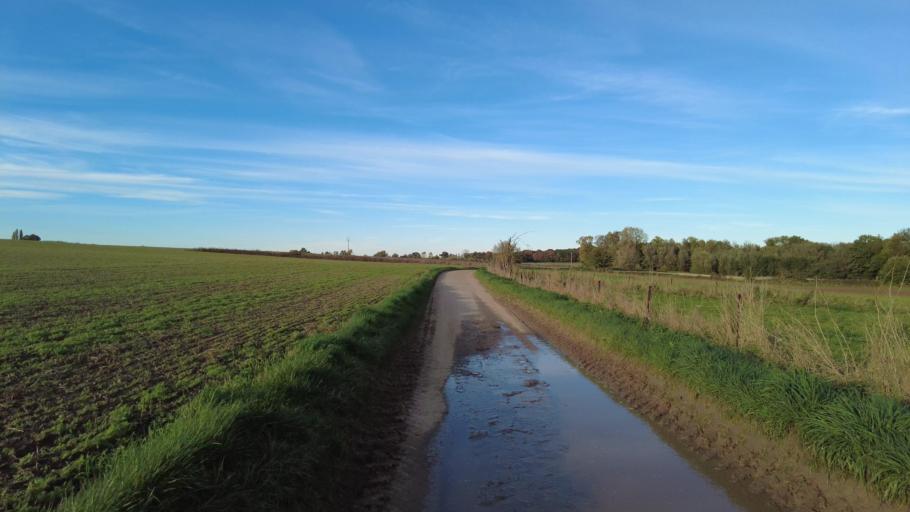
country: BE
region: Flanders
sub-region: Provincie Vlaams-Brabant
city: Hoegaarden
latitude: 50.7256
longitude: 4.9408
